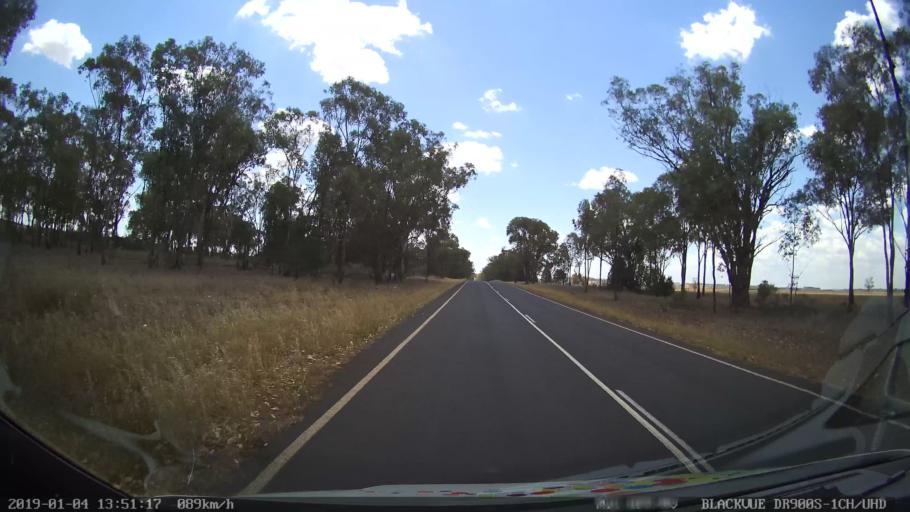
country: AU
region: New South Wales
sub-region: Dubbo Municipality
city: Dubbo
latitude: -32.4091
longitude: 148.5709
